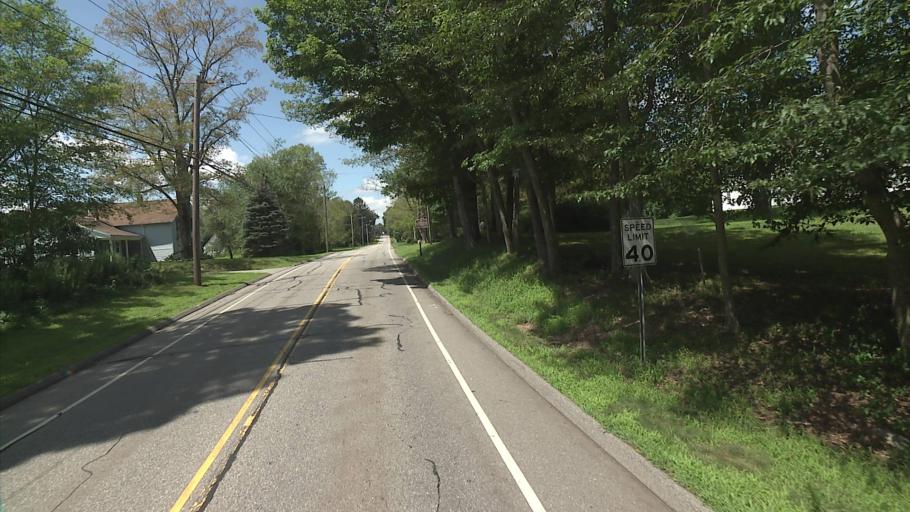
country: US
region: Connecticut
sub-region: Windham County
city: Windham
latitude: 41.6985
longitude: -72.0846
